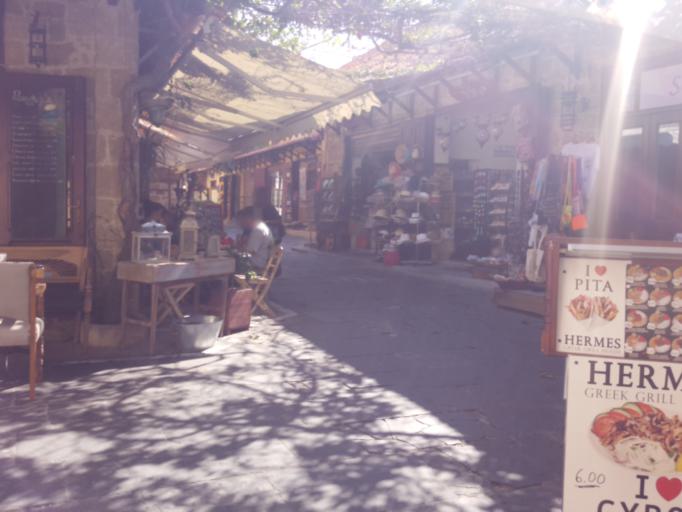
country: GR
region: South Aegean
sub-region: Nomos Dodekanisou
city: Rodos
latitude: 36.4428
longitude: 28.2278
